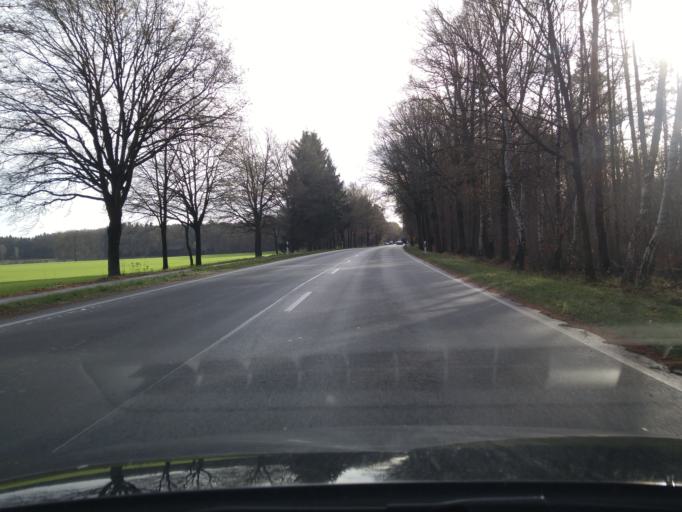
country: DE
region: Lower Saxony
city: Wietzendorf
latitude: 52.9169
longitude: 9.9137
